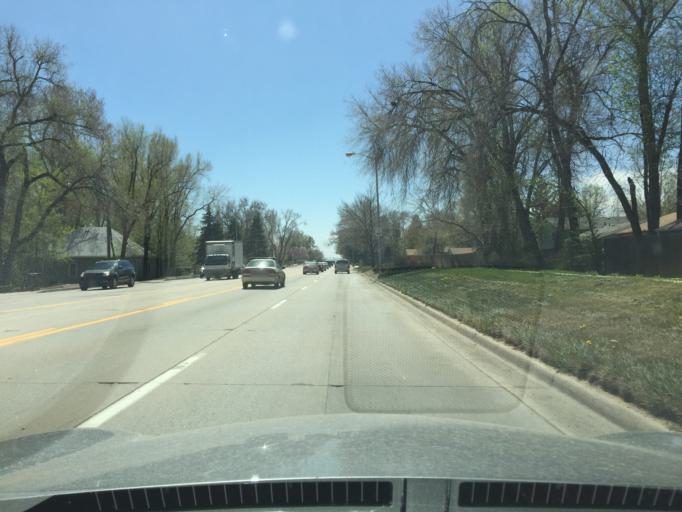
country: US
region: Colorado
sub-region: Boulder County
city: Longmont
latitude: 40.1804
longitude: -105.1310
